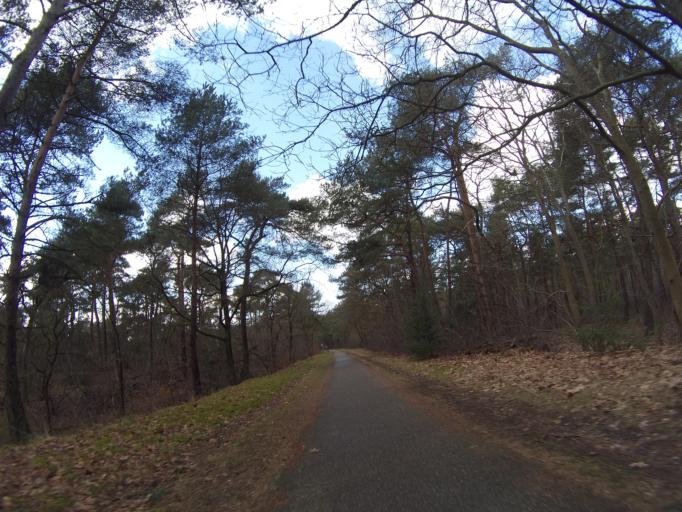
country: NL
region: Utrecht
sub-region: Gemeente Zeist
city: Zeist
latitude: 52.1217
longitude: 5.2344
